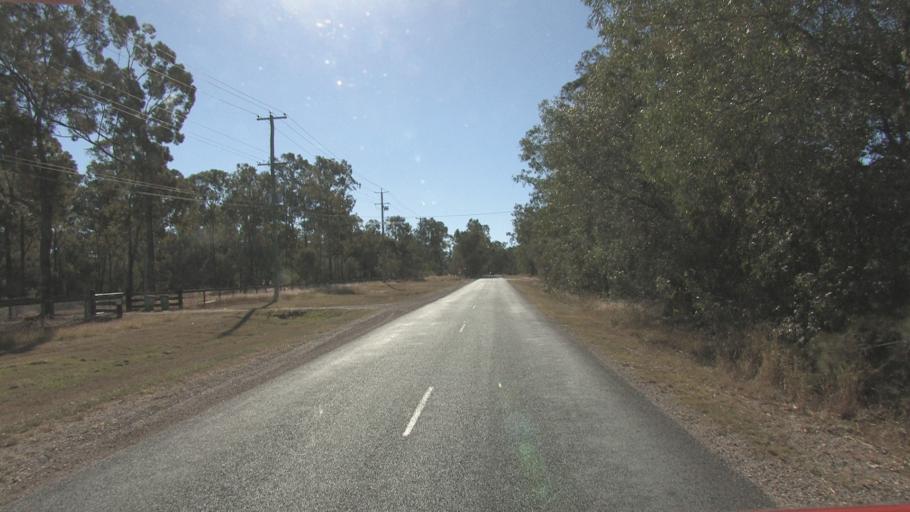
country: AU
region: Queensland
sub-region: Logan
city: North Maclean
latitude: -27.7607
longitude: 152.9962
